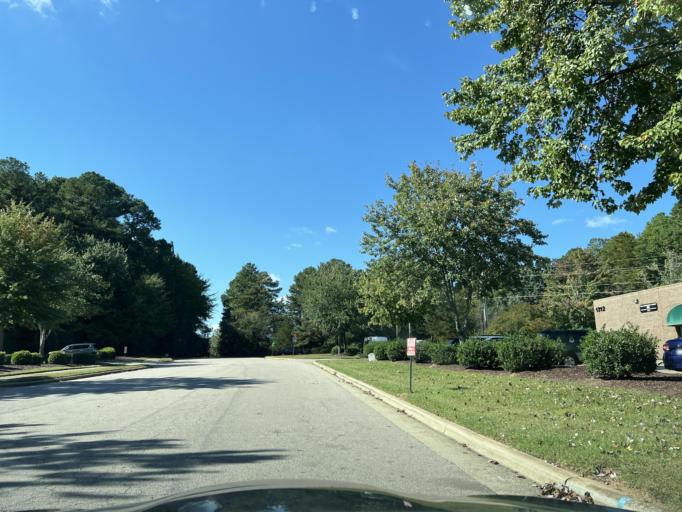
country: US
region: North Carolina
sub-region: Wake County
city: Raleigh
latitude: 35.7535
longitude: -78.6608
